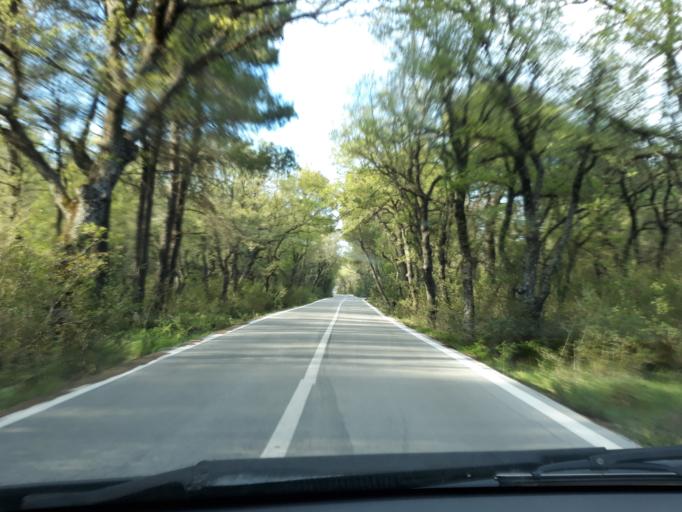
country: GR
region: Attica
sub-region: Nomarchia Anatolikis Attikis
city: Afidnes
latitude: 38.2008
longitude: 23.7867
